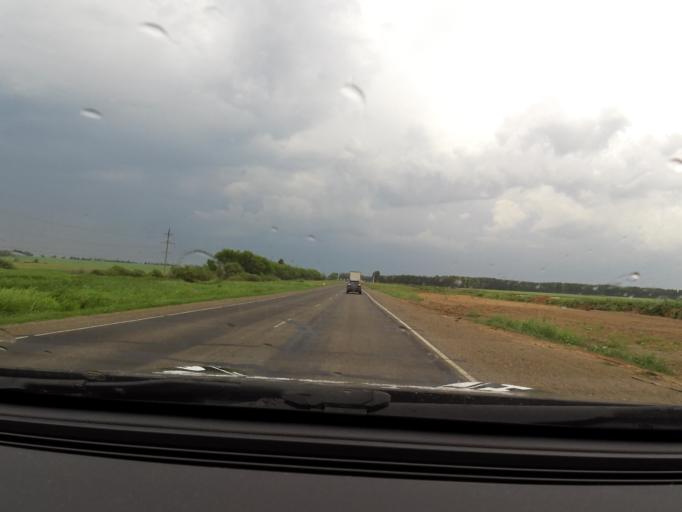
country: RU
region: Bashkortostan
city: Asanovo
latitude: 54.9139
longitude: 55.5925
